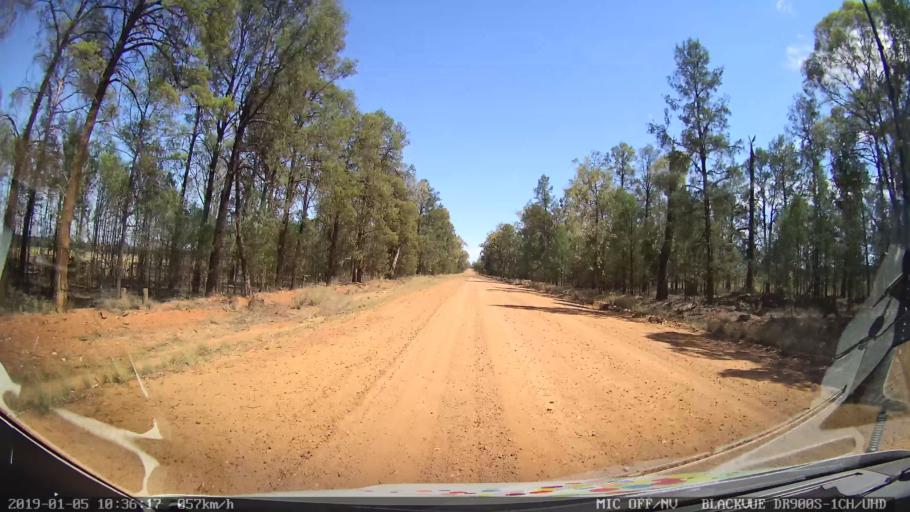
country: AU
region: New South Wales
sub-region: Gilgandra
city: Gilgandra
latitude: -31.4833
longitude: 148.9256
